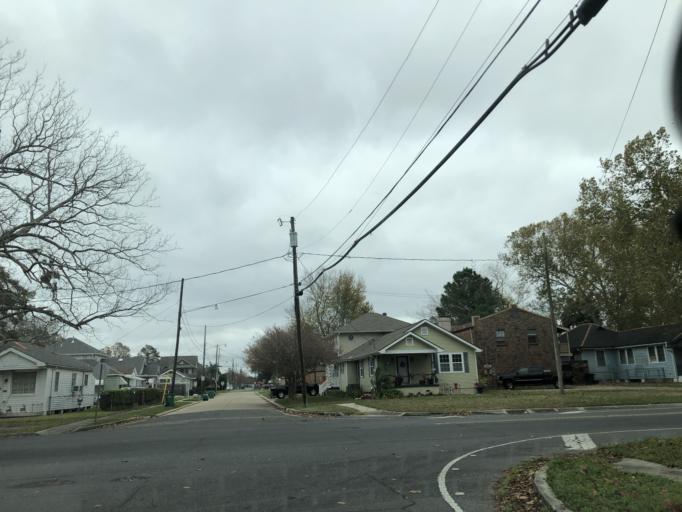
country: US
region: Louisiana
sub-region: Jefferson Parish
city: Metairie Terrace
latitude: 29.9807
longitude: -90.1605
